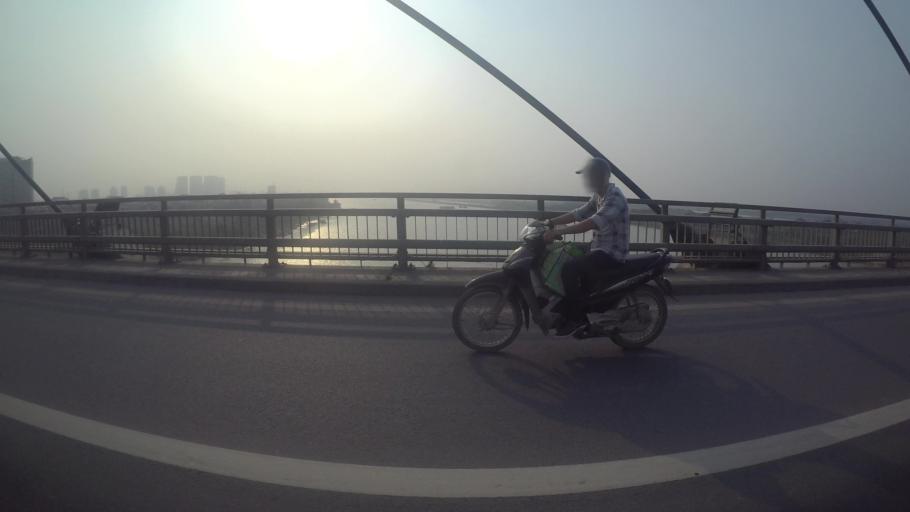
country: VN
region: Ha Noi
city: Tay Ho
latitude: 21.0896
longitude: 105.8189
